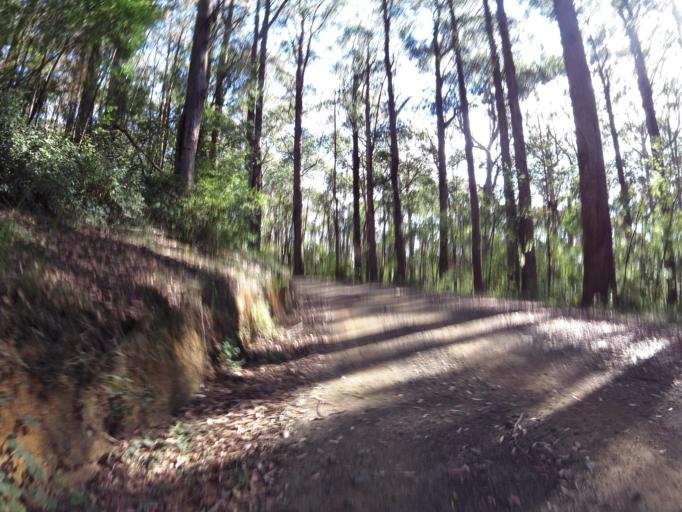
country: AU
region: Victoria
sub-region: Yarra Ranges
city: Millgrove
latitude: -37.8497
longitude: 145.7980
